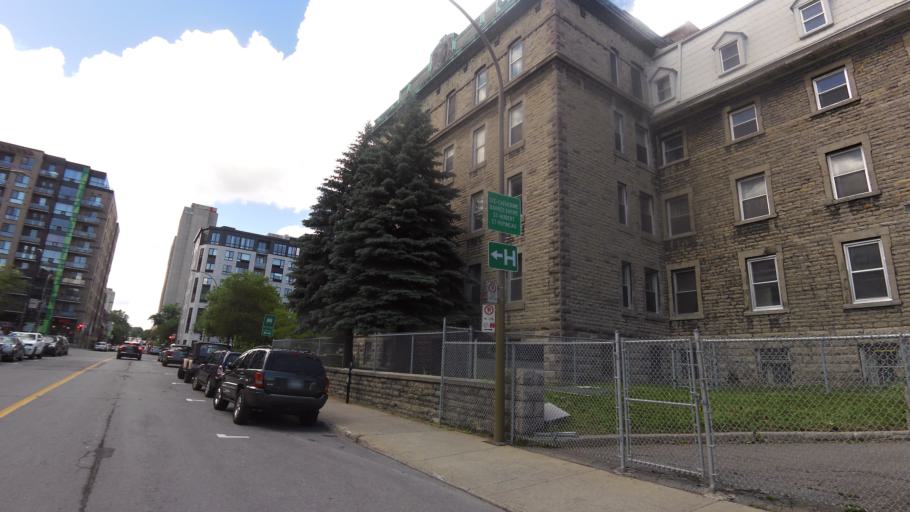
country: CA
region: Quebec
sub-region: Montreal
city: Montreal
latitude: 45.5140
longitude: -73.5557
